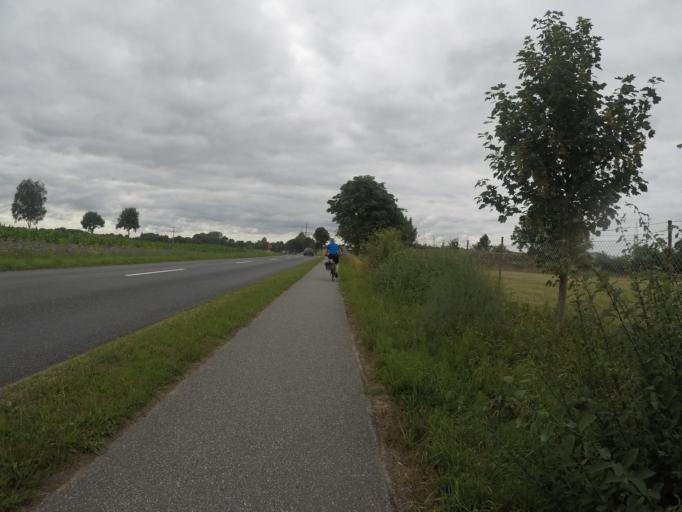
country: DE
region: Lower Saxony
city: Hemmoor
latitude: 53.6940
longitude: 9.1335
